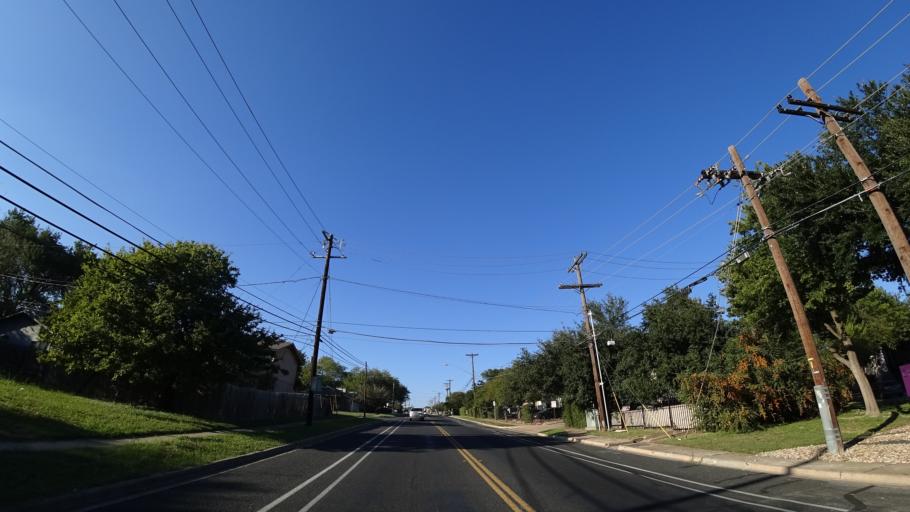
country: US
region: Texas
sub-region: Travis County
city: Austin
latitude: 30.2274
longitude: -97.7354
